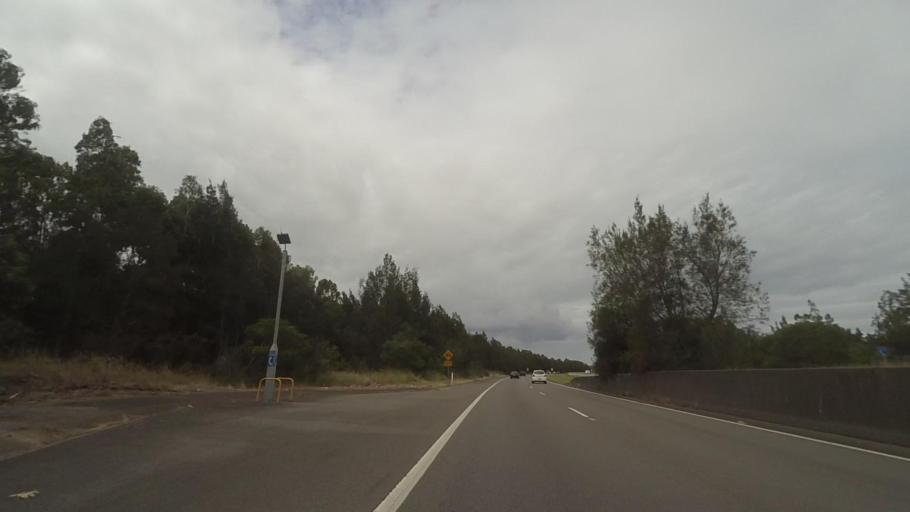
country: AU
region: New South Wales
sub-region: Port Stephens Shire
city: Raymond Terrace
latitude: -32.7481
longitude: 151.7683
